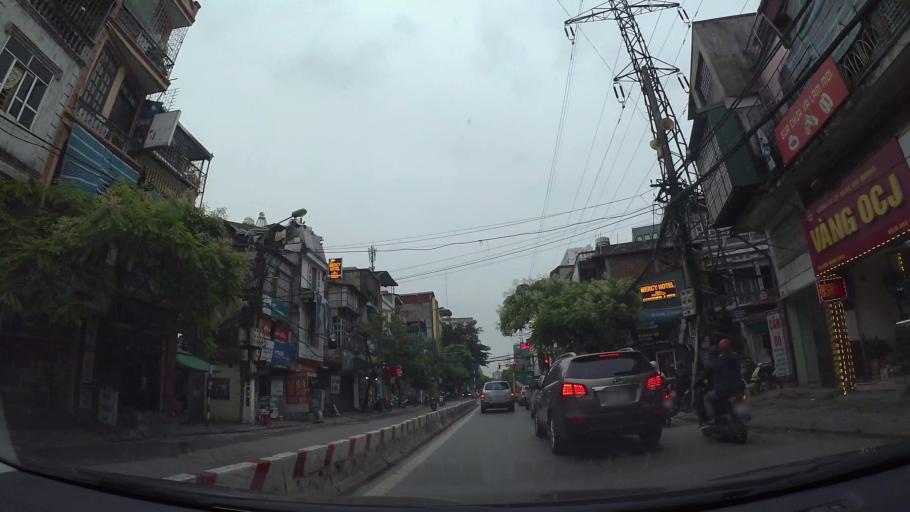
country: VN
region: Ha Noi
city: Hai BaTrung
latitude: 21.0036
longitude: 105.8694
